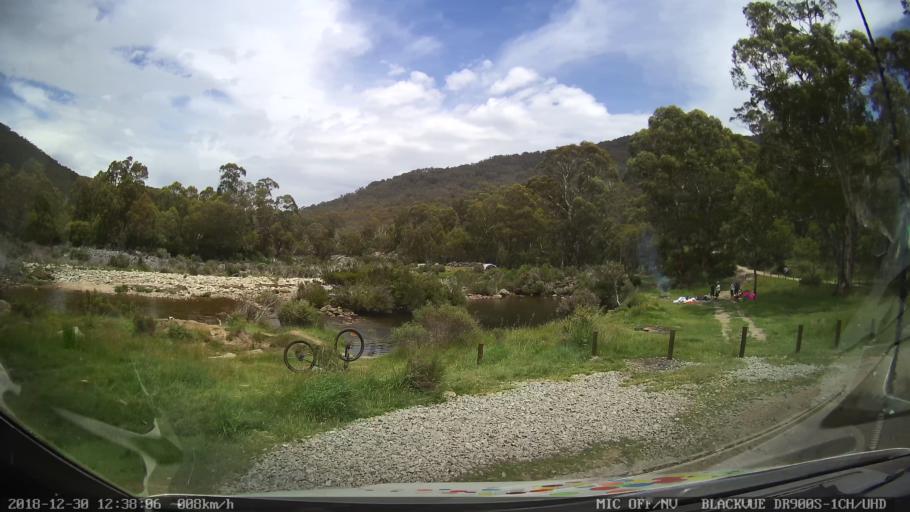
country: AU
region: New South Wales
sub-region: Snowy River
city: Jindabyne
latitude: -36.3226
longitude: 148.4658
